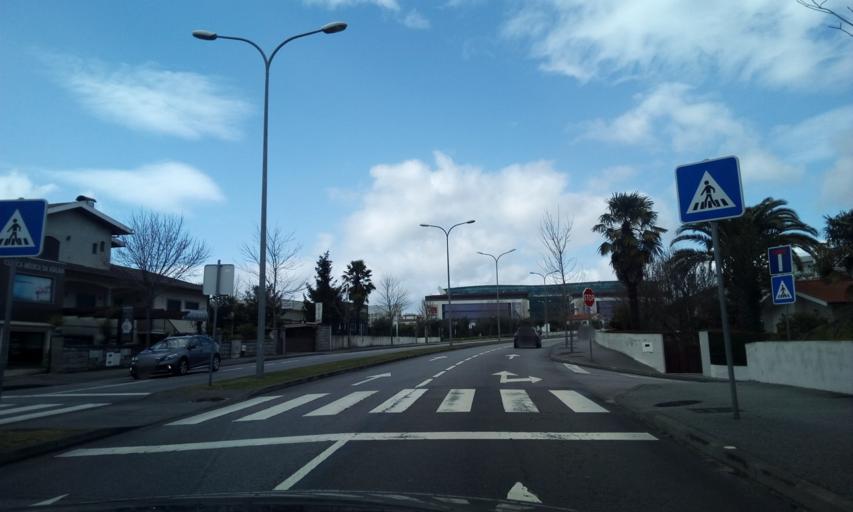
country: PT
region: Viseu
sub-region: Viseu
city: Viseu
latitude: 40.6392
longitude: -7.9092
